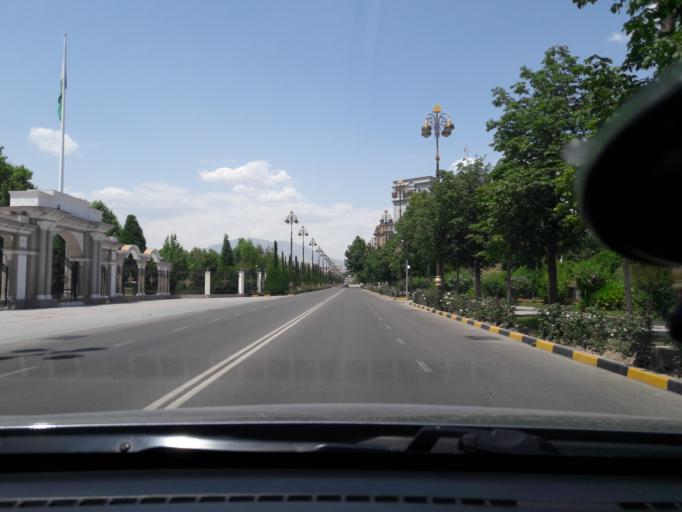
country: TJ
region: Dushanbe
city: Dushanbe
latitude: 38.5759
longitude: 68.7822
